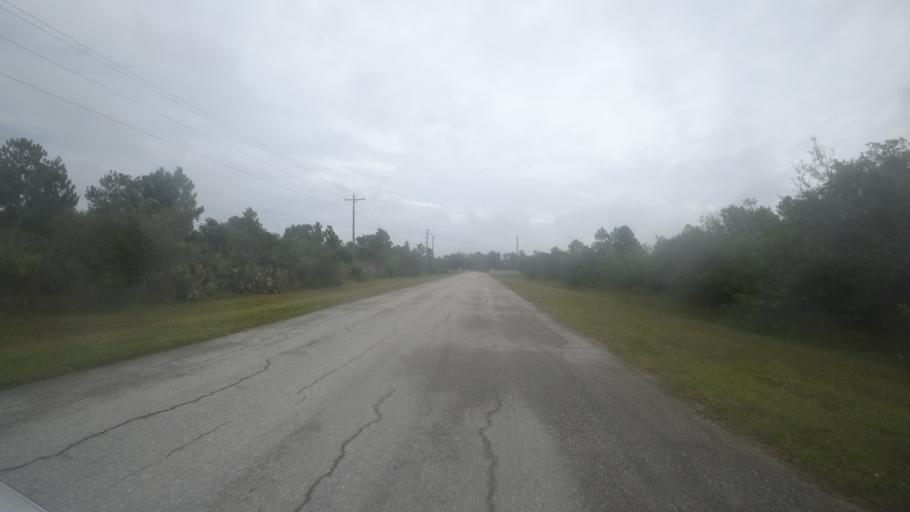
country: US
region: Florida
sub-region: Sarasota County
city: The Meadows
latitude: 27.4050
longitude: -82.3402
